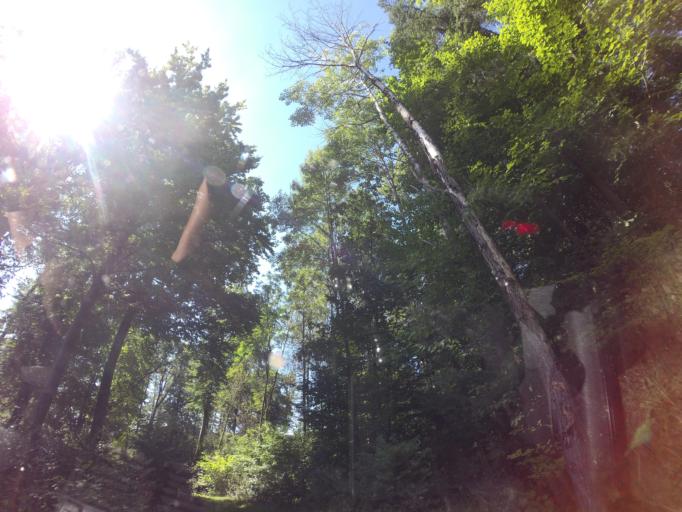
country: PL
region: West Pomeranian Voivodeship
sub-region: Powiat choszczenski
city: Recz
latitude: 53.2276
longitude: 15.6451
